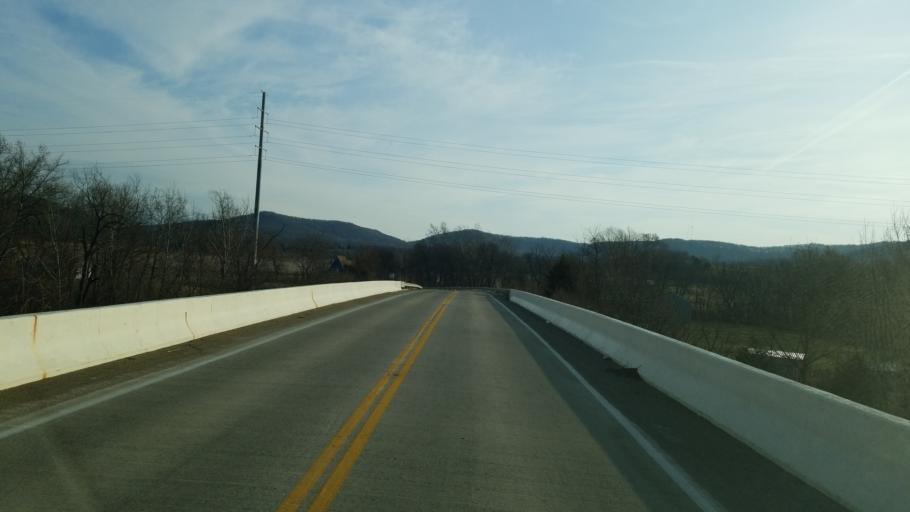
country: US
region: Ohio
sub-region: Ross County
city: Chillicothe
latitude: 39.3849
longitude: -82.9657
